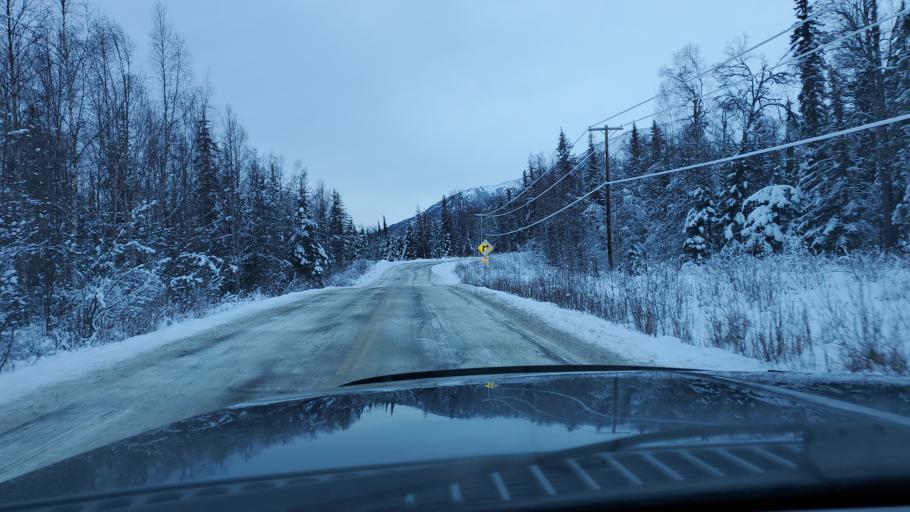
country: US
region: Alaska
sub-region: Matanuska-Susitna Borough
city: Lakes
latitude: 61.6933
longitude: -149.3198
